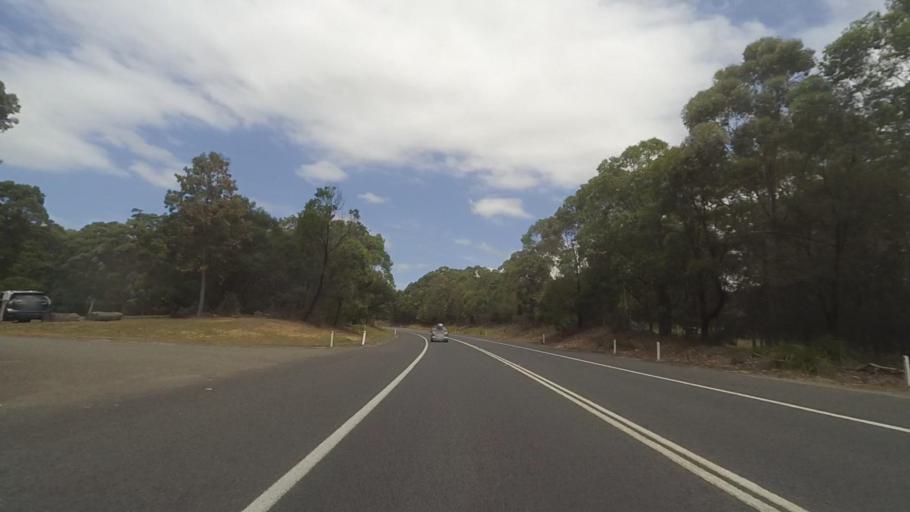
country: AU
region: New South Wales
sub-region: Shoalhaven Shire
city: Milton
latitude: -35.2341
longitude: 150.4312
